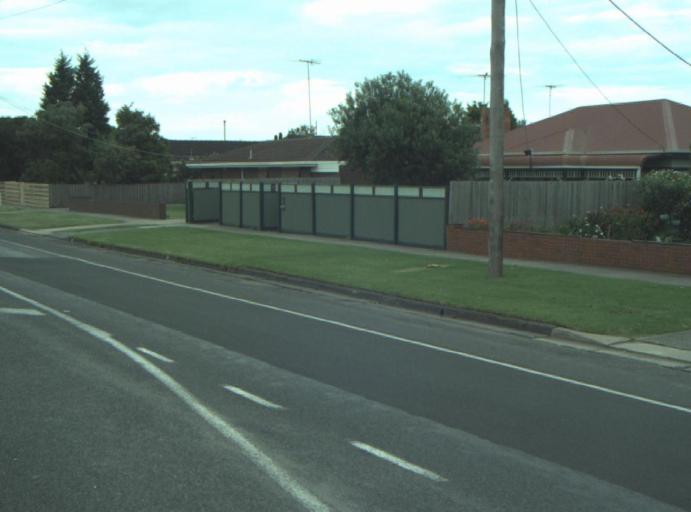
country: AU
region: Victoria
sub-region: Greater Geelong
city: East Geelong
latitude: -38.1598
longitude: 144.3862
